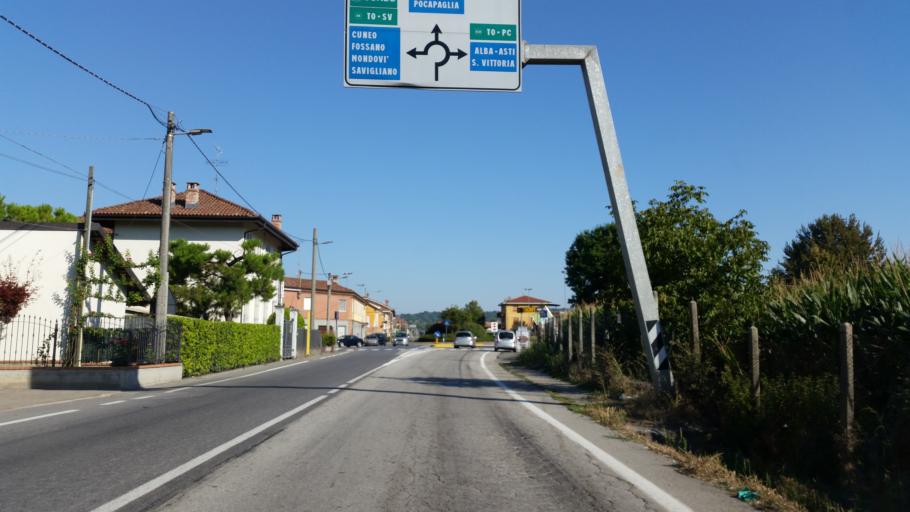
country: IT
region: Piedmont
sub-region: Provincia di Cuneo
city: Cinzano
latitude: 44.6858
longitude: 7.8968
